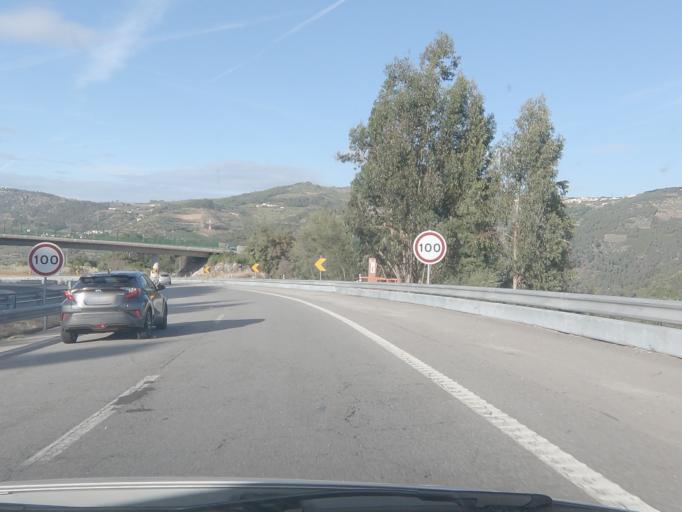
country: PT
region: Viseu
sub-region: Lamego
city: Lamego
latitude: 41.0888
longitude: -7.7852
